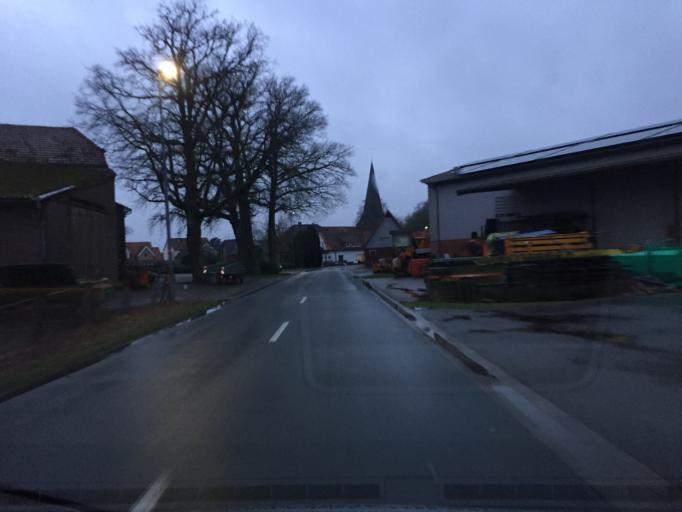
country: DE
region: Lower Saxony
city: Sustedt
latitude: 52.8808
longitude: 8.8741
